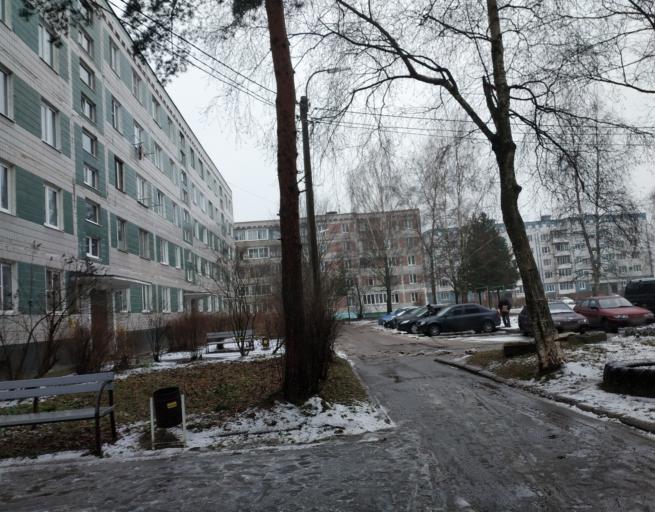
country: RU
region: Moskovskaya
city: Taldom
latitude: 56.7429
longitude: 37.5310
